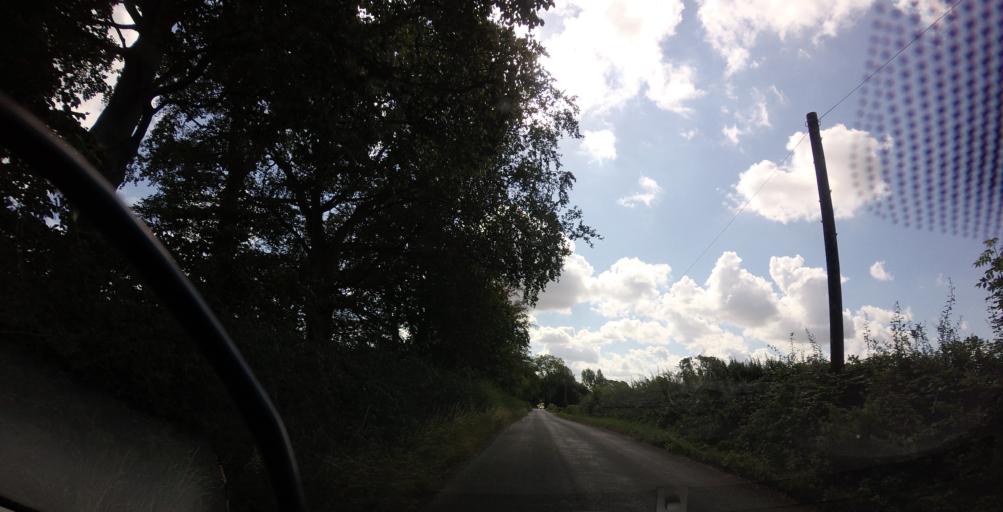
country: GB
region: England
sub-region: North Yorkshire
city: Boroughbridge
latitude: 54.0478
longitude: -1.4180
